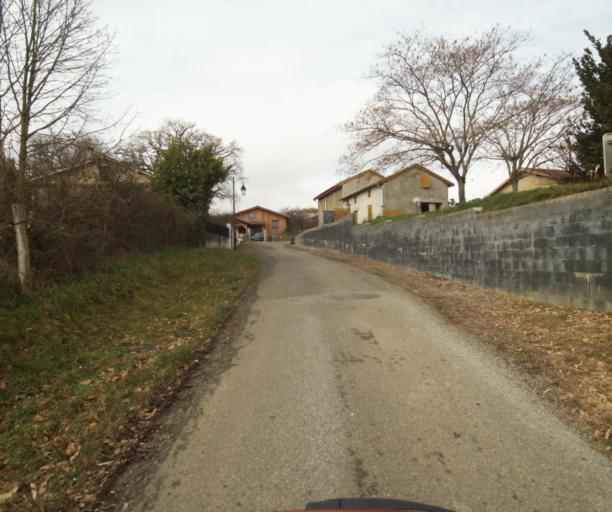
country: FR
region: Midi-Pyrenees
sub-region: Departement de l'Ariege
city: Pamiers
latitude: 43.1052
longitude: 1.5167
